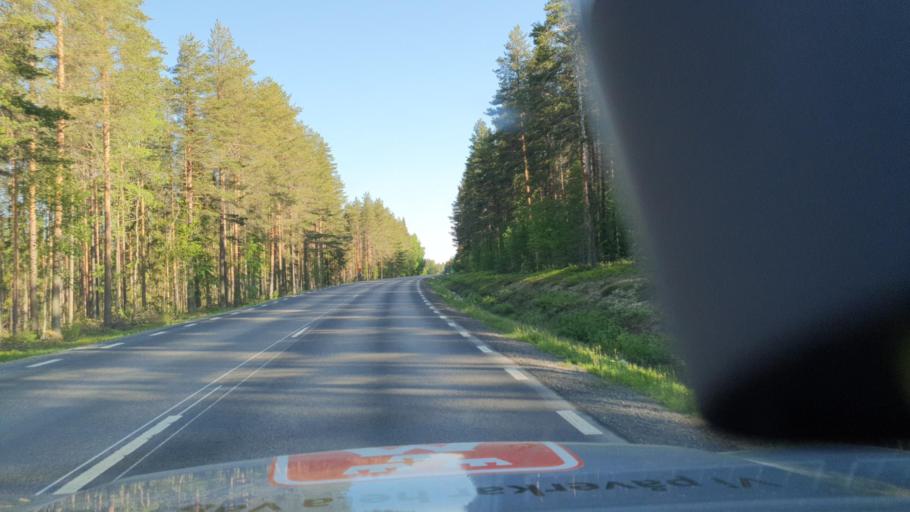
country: SE
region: Norrbotten
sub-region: Bodens Kommun
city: Boden
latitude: 65.8672
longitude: 21.4155
